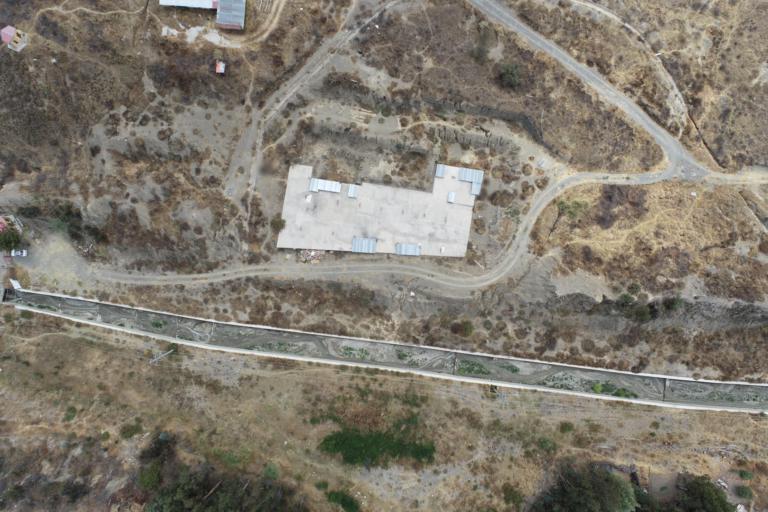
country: BO
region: La Paz
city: La Paz
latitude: -16.5369
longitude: -68.0686
